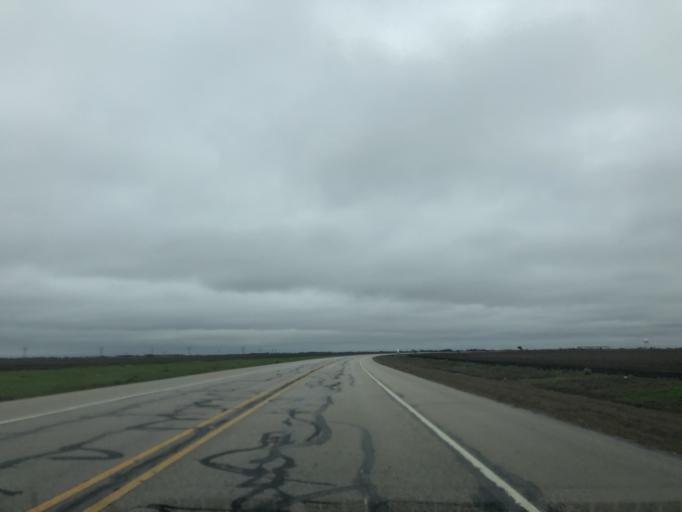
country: US
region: Texas
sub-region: Williamson County
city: Hutto
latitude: 30.5986
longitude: -97.5330
